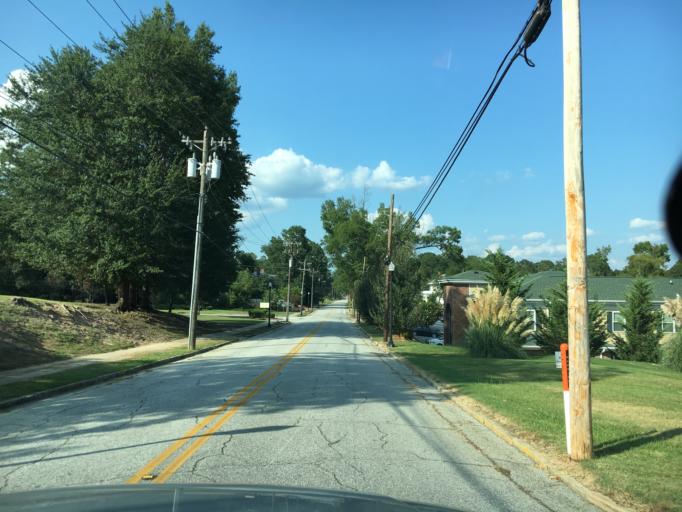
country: US
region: South Carolina
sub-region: Laurens County
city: Clinton
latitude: 34.4761
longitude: -81.8793
